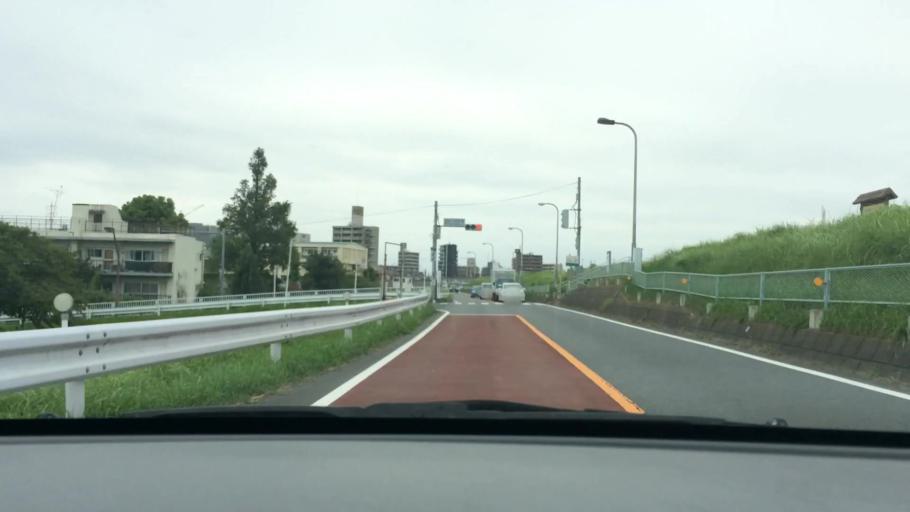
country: JP
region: Chiba
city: Matsudo
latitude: 35.7643
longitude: 139.8791
